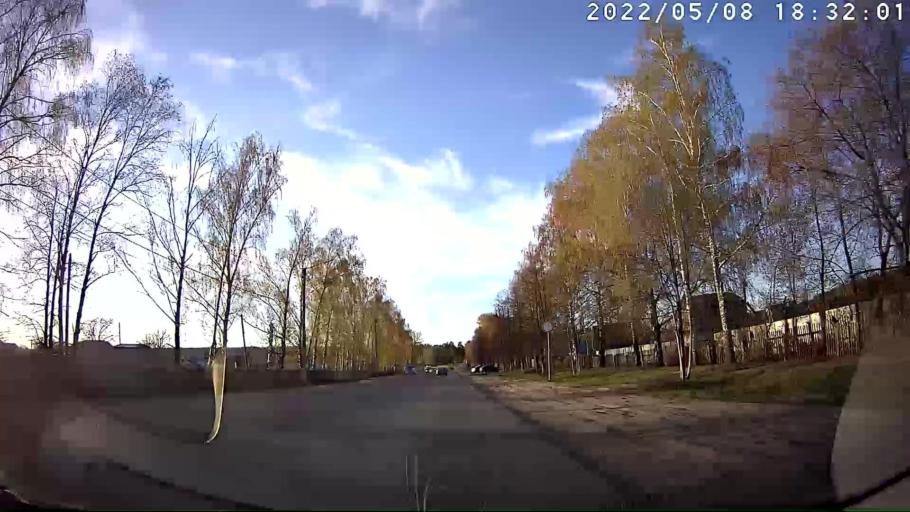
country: RU
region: Mariy-El
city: Volzhsk
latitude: 55.8845
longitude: 48.3598
